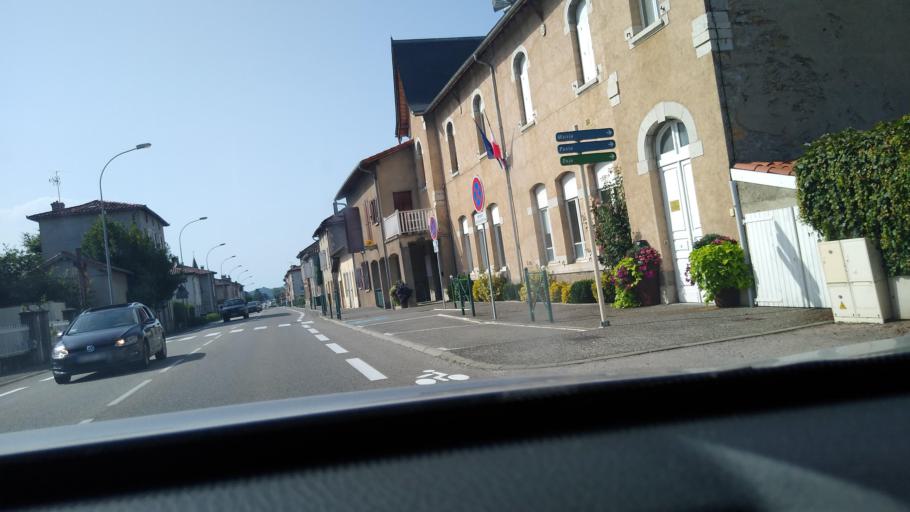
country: FR
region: Midi-Pyrenees
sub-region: Departement de l'Ariege
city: Saint-Lizier
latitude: 43.0081
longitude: 1.1217
